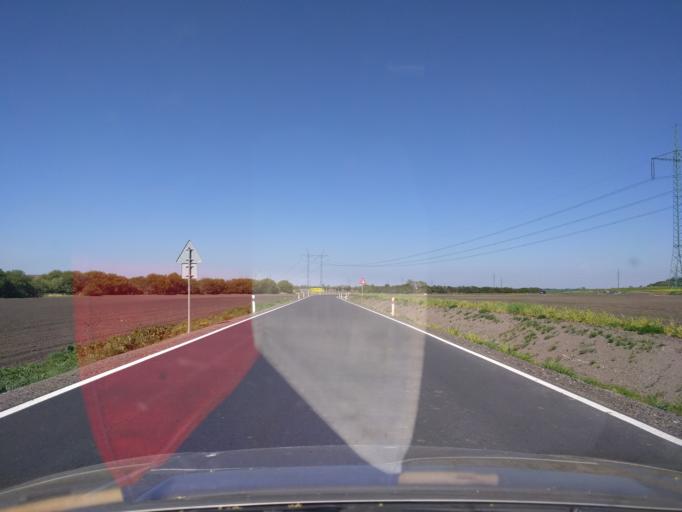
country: CZ
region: Central Bohemia
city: Cesky Brod
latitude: 50.1157
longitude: 14.8605
